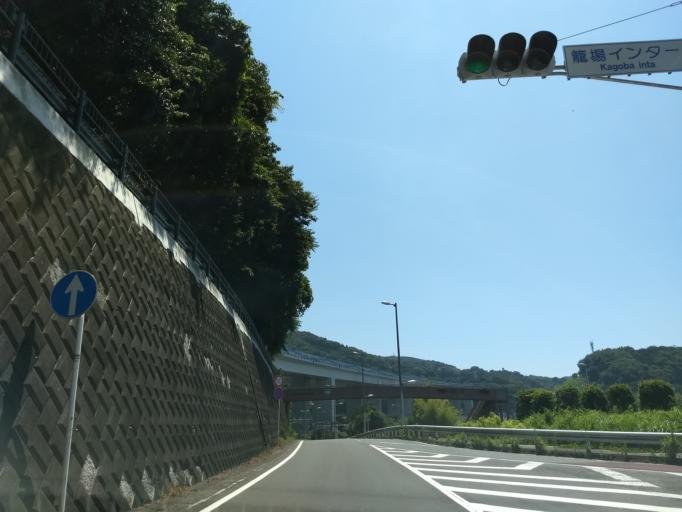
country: JP
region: Kanagawa
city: Hadano
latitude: 35.3483
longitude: 139.1461
